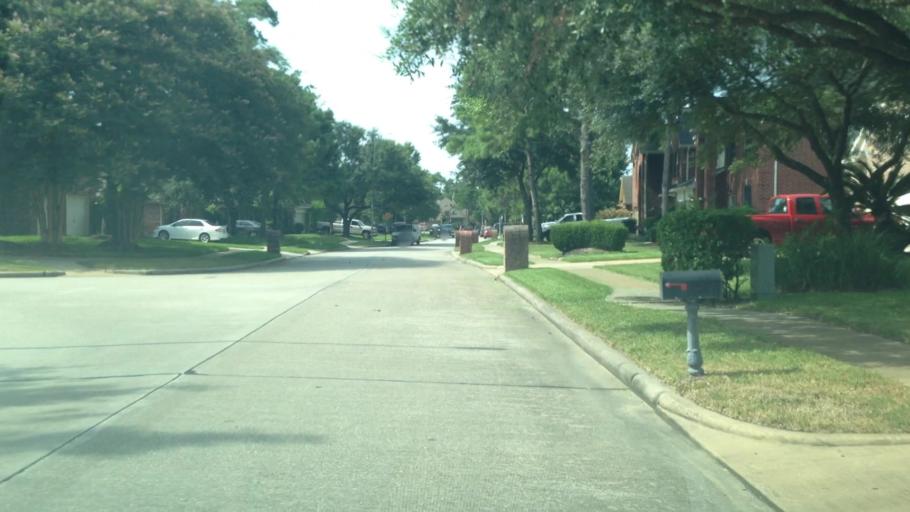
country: US
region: Texas
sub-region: Harris County
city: Atascocita
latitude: 29.9316
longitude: -95.1754
